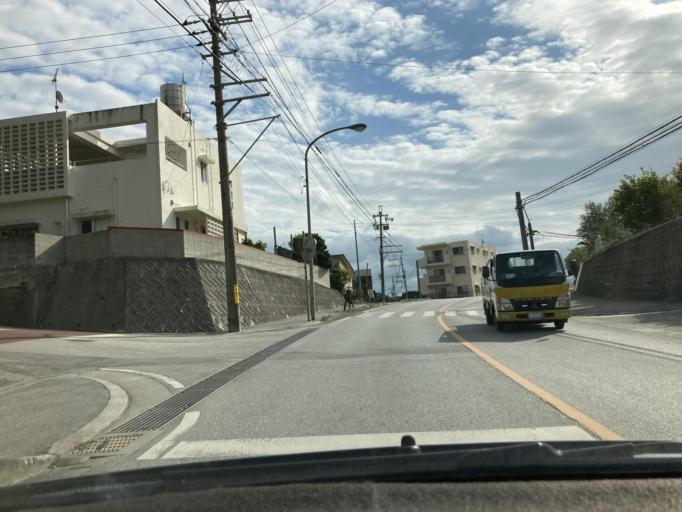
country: JP
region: Okinawa
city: Nago
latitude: 26.6202
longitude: 127.9995
